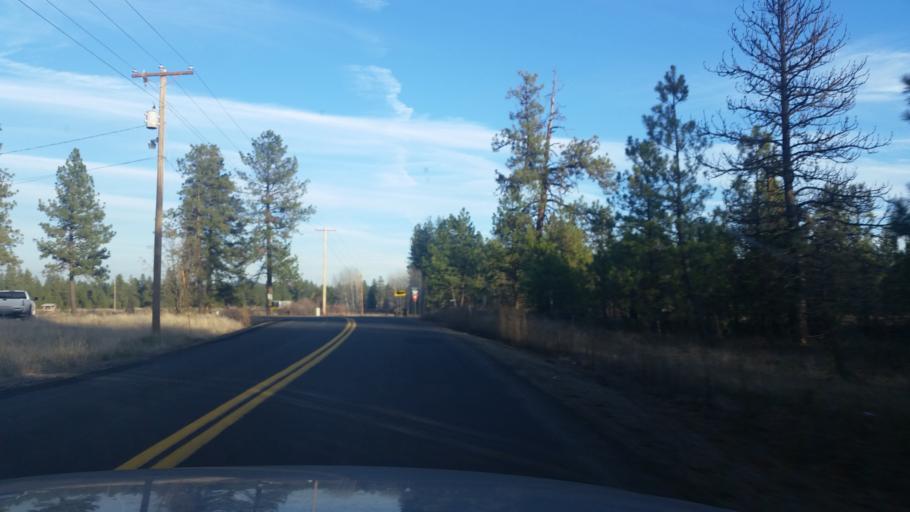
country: US
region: Washington
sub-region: Spokane County
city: Cheney
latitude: 47.5149
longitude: -117.4571
